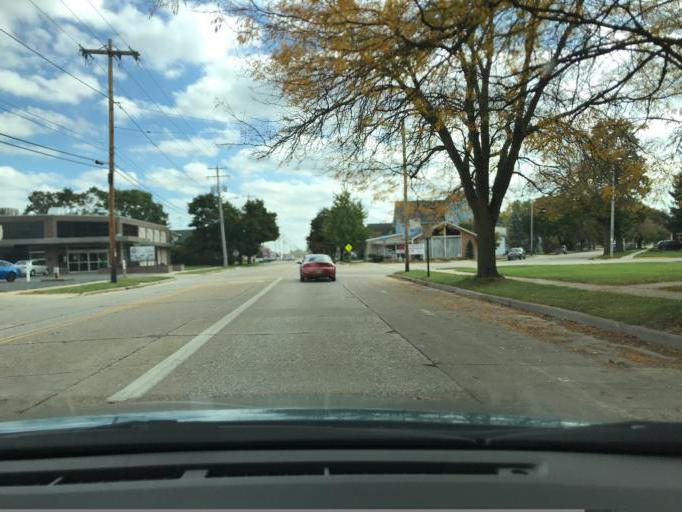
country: US
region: Wisconsin
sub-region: Racine County
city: Burlington
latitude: 42.6751
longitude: -88.2731
